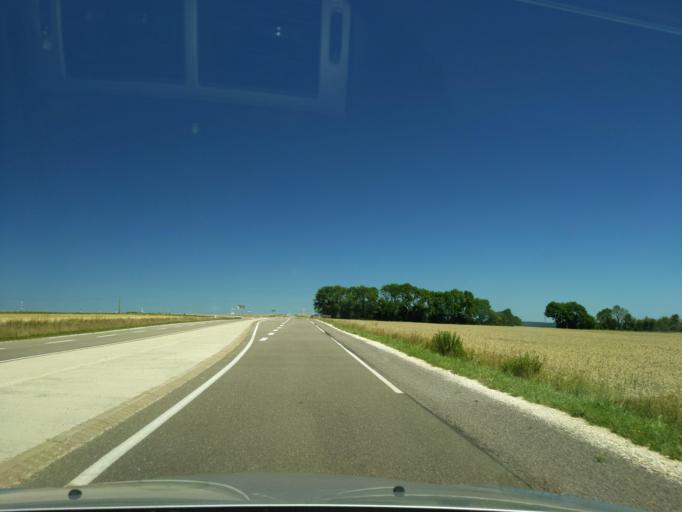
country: FR
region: Bourgogne
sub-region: Departement de la Cote-d'Or
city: Is-sur-Tille
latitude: 47.4944
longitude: 5.0918
